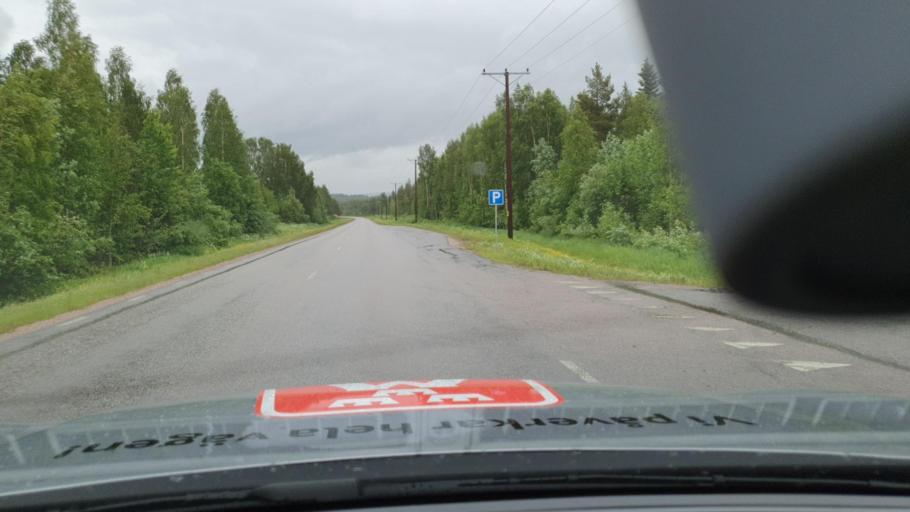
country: SE
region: Norrbotten
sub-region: Overtornea Kommun
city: OEvertornea
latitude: 66.3958
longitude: 23.5926
